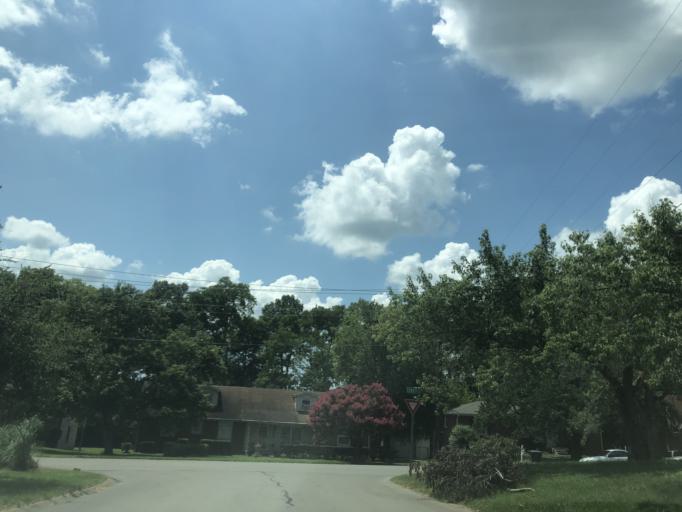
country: US
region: Tennessee
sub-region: Davidson County
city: Lakewood
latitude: 36.1969
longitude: -86.6138
